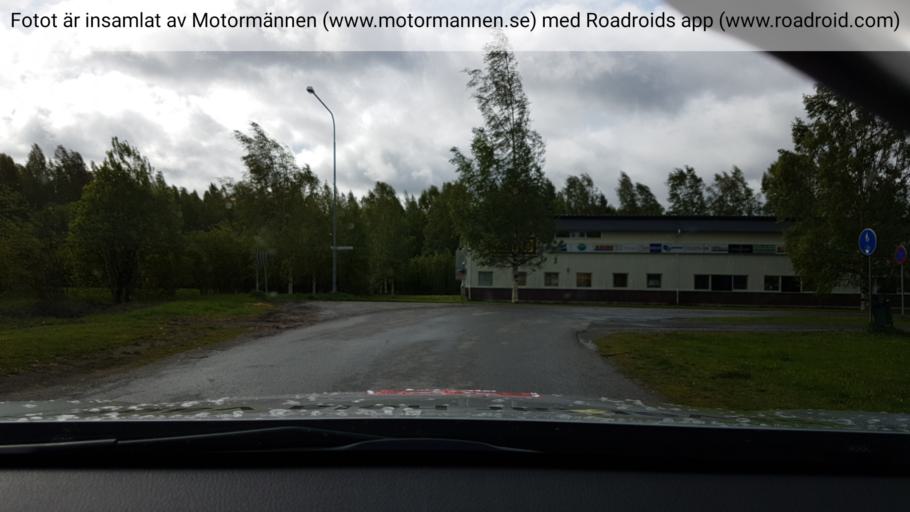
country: SE
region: Vaesterbotten
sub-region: Skelleftea Kommun
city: Skelleftea
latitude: 64.7393
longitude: 20.9906
